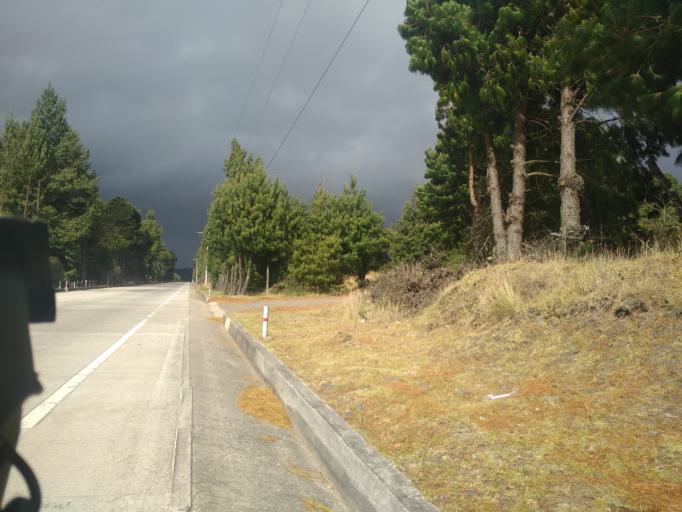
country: EC
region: Azuay
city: Cuenca
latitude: -3.3505
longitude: -79.1849
